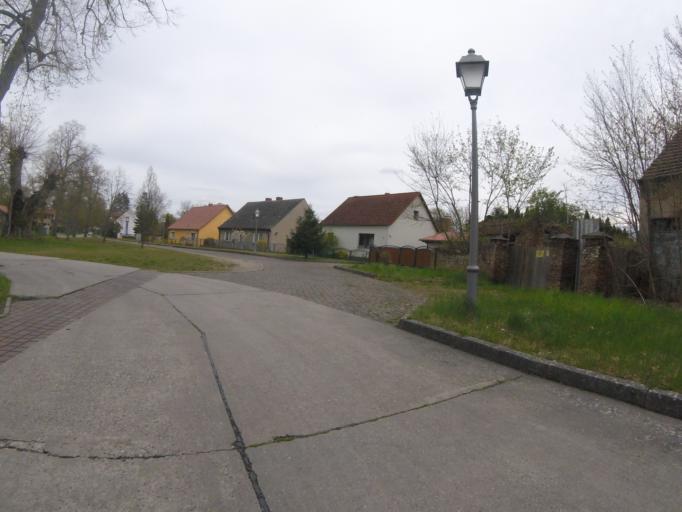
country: DE
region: Brandenburg
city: Bestensee
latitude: 52.2245
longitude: 13.6548
